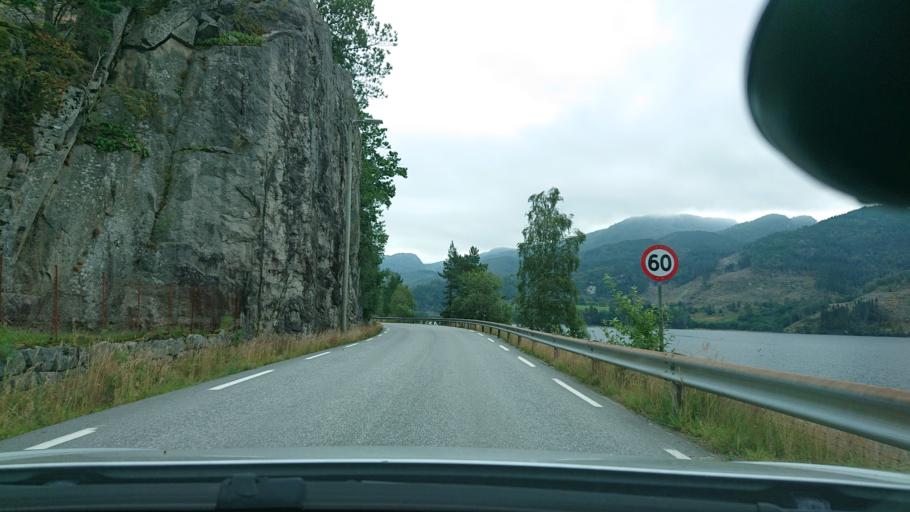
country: NO
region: Rogaland
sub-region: Hjelmeland
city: Hjelmelandsvagen
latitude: 59.2319
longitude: 6.1906
